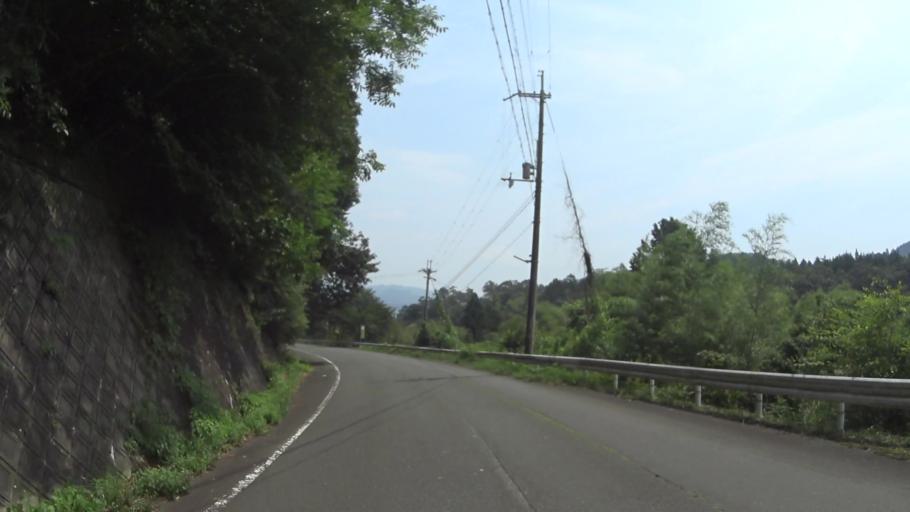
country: JP
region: Kyoto
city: Ayabe
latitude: 35.2056
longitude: 135.3890
